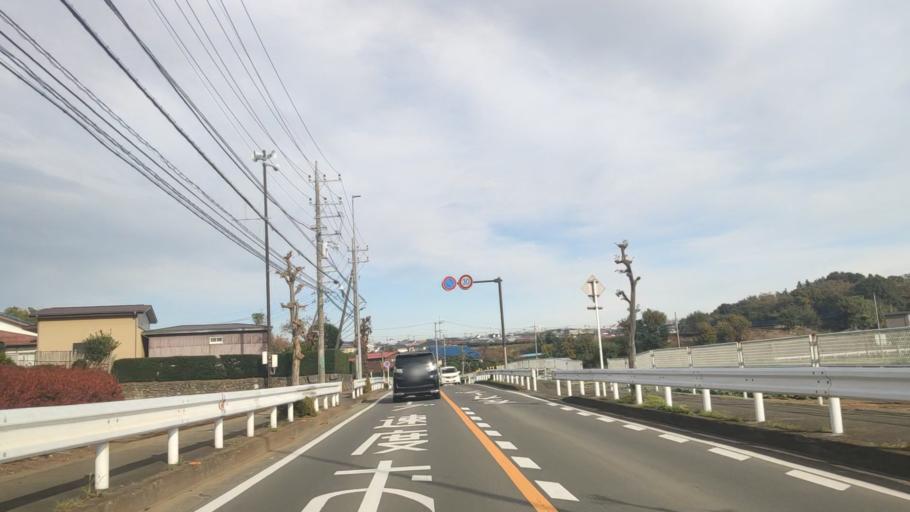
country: JP
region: Kanagawa
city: Atsugi
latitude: 35.4303
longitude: 139.4035
